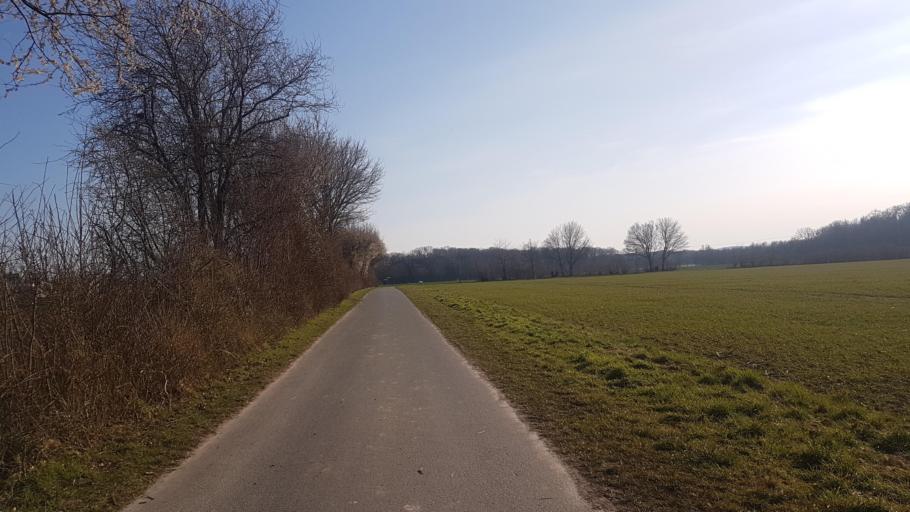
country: DE
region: Lower Saxony
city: Hemmingen
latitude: 52.3170
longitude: 9.7027
